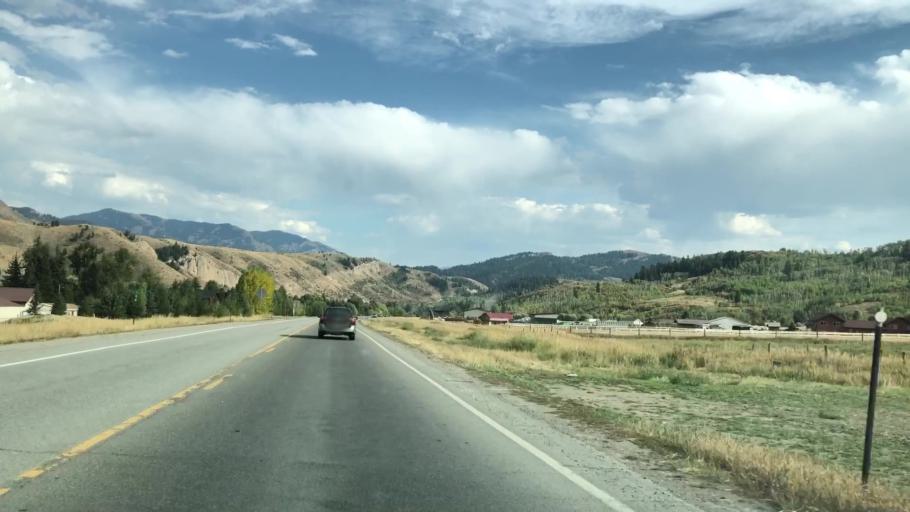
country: US
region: Wyoming
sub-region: Teton County
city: South Park
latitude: 43.3700
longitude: -110.7386
